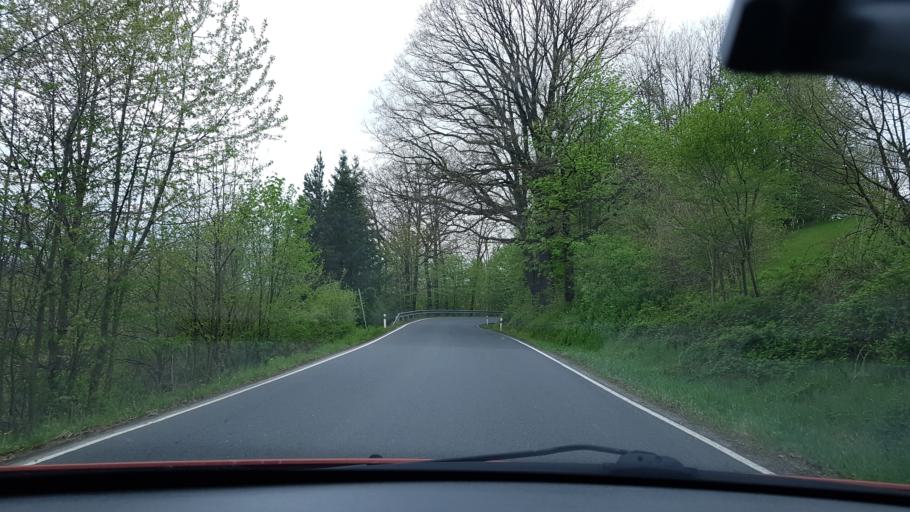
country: CZ
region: Olomoucky
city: Mikulovice
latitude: 50.3051
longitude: 17.3215
